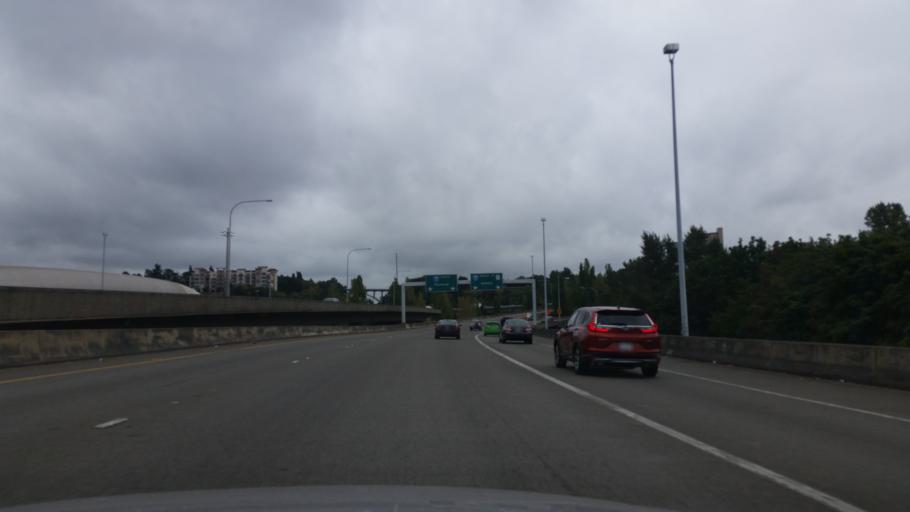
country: US
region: Washington
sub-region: Pierce County
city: Tacoma
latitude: 47.2379
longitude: -122.4323
